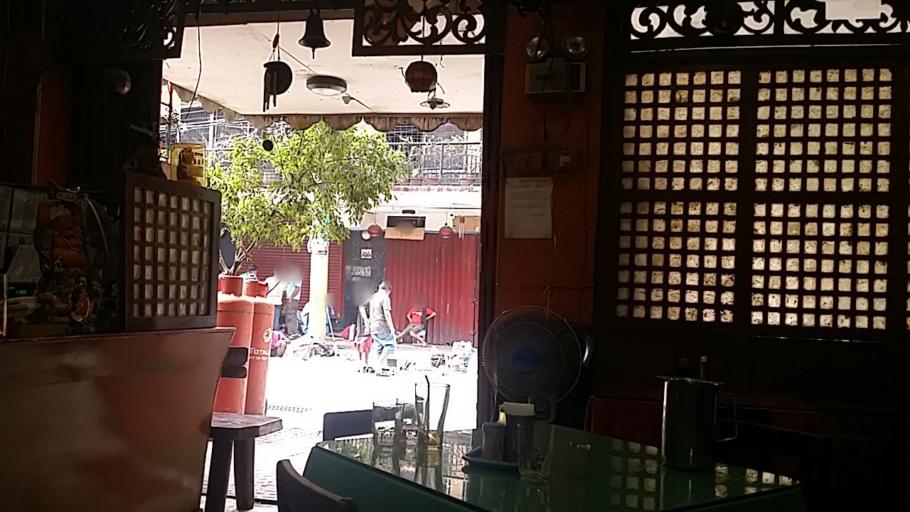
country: PH
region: Metro Manila
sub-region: City of Manila
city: Manila
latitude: 14.6033
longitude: 120.9809
